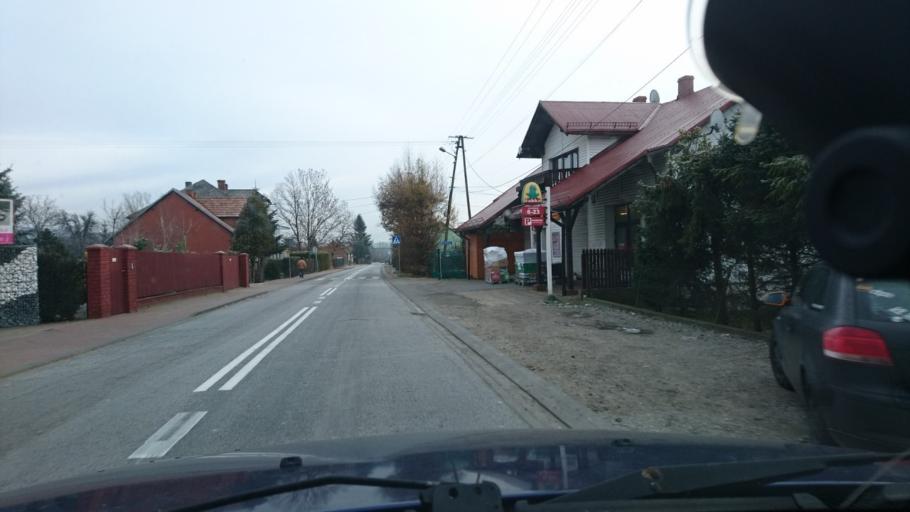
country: PL
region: Silesian Voivodeship
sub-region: Powiat bielski
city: Rybarzowice
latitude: 49.7291
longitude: 19.1095
